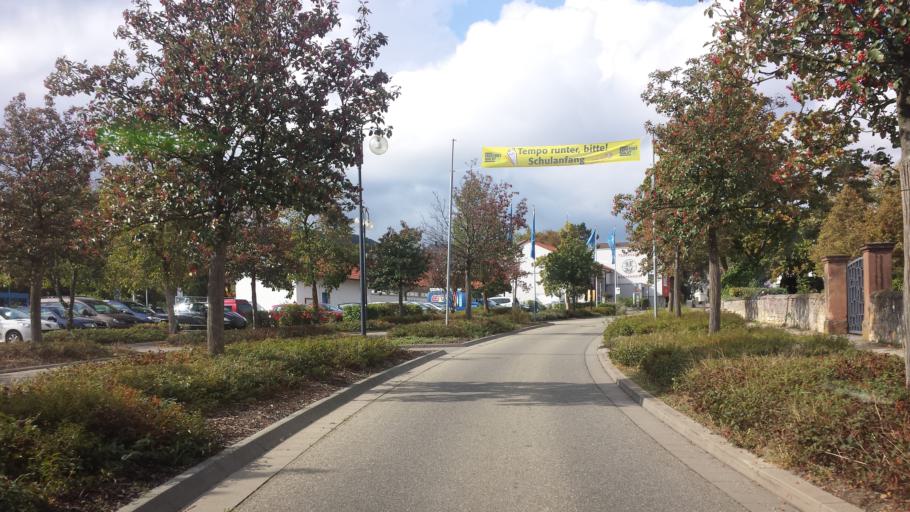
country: DE
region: Rheinland-Pfalz
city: Wachenheim
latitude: 49.4421
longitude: 8.1830
